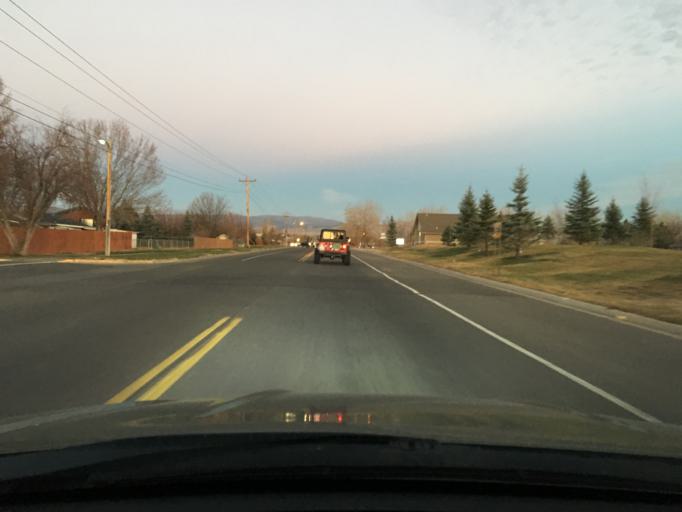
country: US
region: Colorado
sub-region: Montrose County
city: Montrose
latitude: 38.4672
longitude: -107.8589
